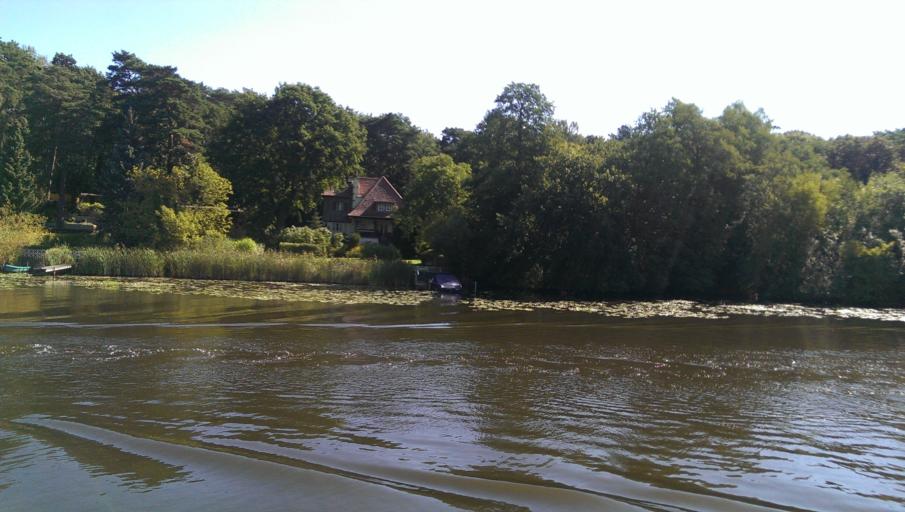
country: DE
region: Berlin
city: Wannsee
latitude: 52.4078
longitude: 13.1409
